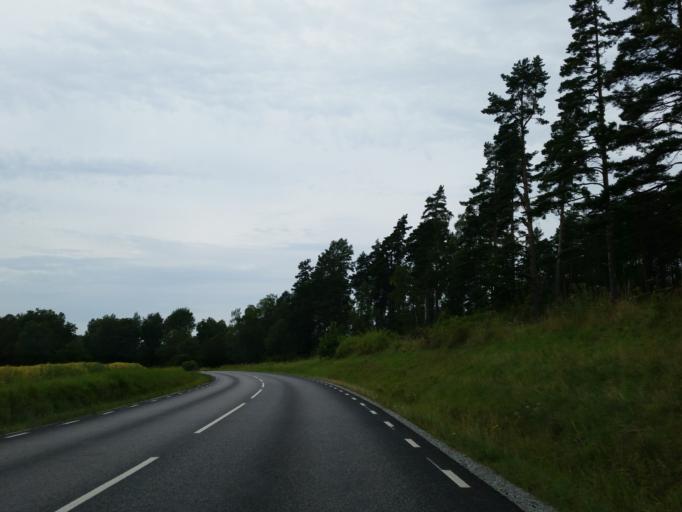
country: SE
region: Stockholm
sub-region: Salems Kommun
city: Ronninge
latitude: 59.2294
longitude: 17.7204
